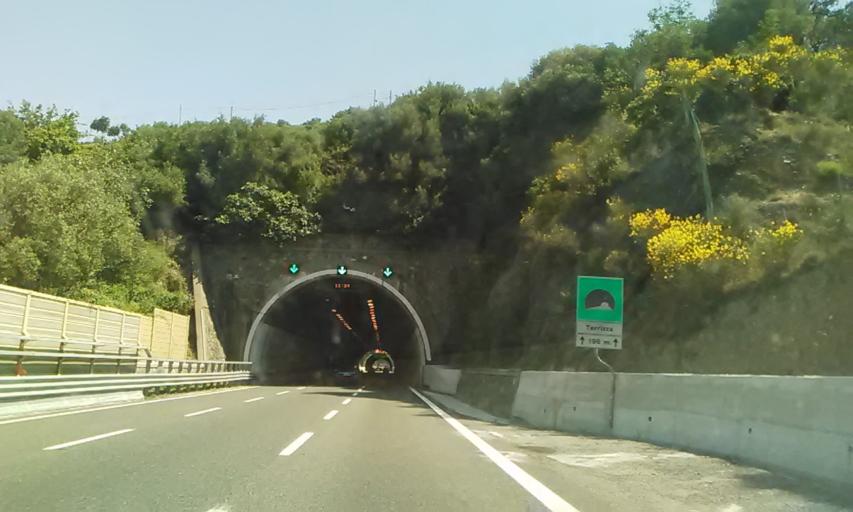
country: IT
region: Liguria
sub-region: Provincia di Savona
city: Celle Ligure
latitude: 44.3398
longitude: 8.5362
